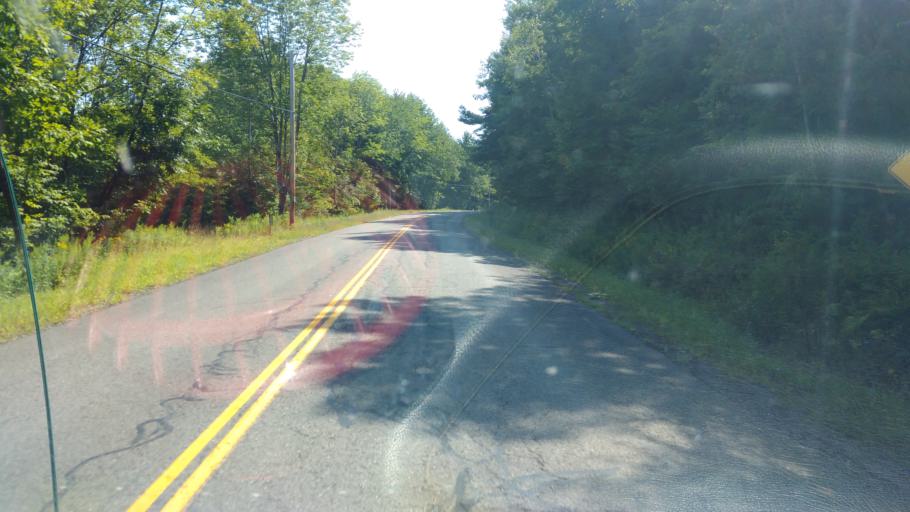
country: US
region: New York
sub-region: Allegany County
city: Belmont
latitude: 42.2906
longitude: -77.9997
